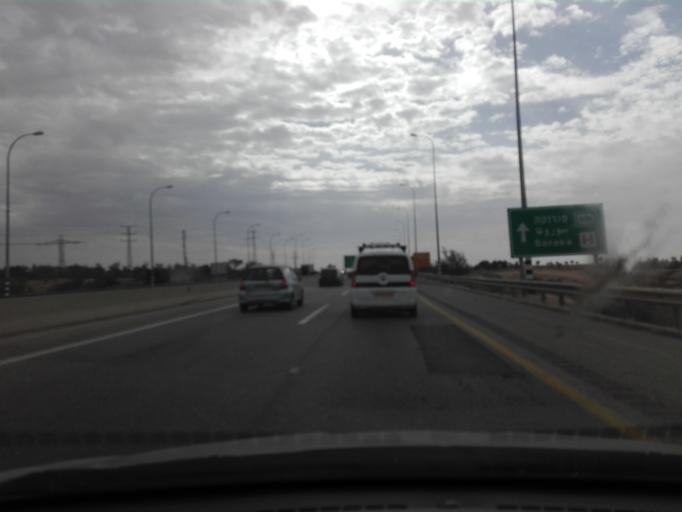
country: IL
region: Southern District
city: Lehavim
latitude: 31.3160
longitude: 34.7876
